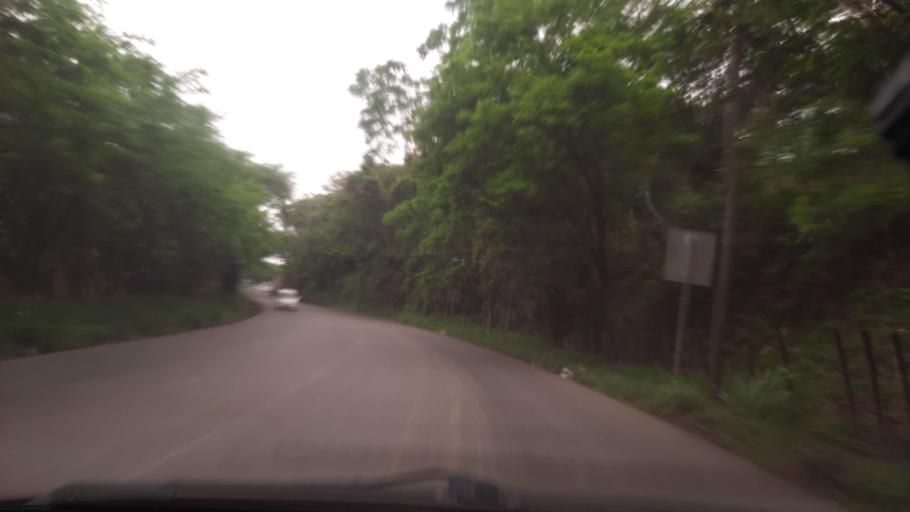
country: GT
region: Izabal
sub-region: Municipio de Los Amates
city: Los Amates
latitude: 15.2546
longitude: -89.1175
